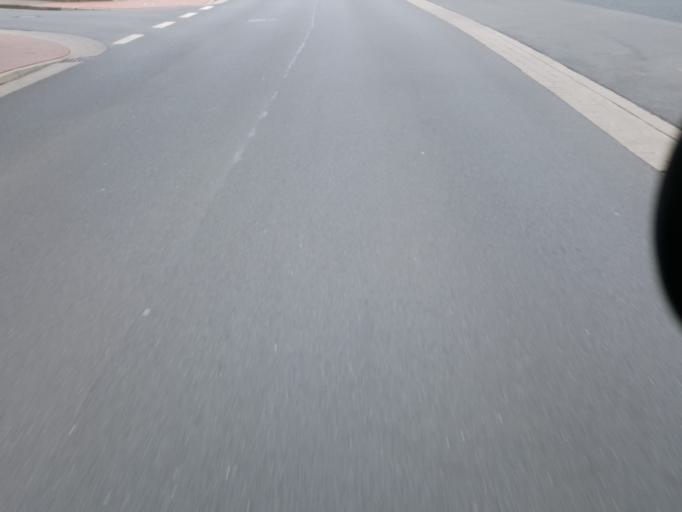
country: DE
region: Lower Saxony
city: Stolzenau
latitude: 52.5106
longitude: 9.0650
